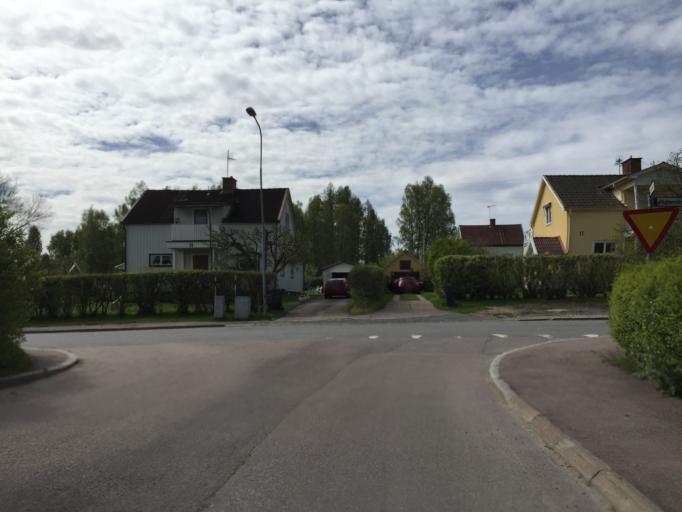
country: SE
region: Dalarna
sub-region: Ludvika Kommun
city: Ludvika
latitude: 60.1257
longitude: 15.1873
